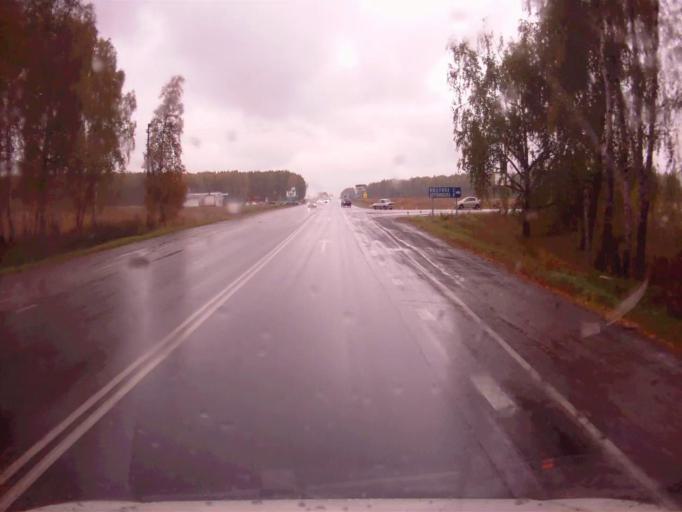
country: RU
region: Chelyabinsk
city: Argayash
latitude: 55.4158
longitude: 61.0293
